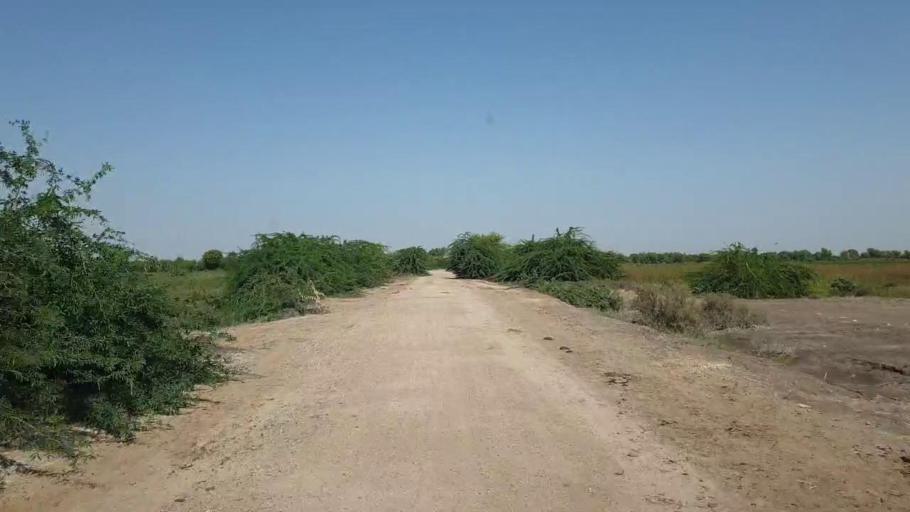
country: PK
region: Sindh
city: Tando Bago
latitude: 24.7374
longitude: 69.0429
